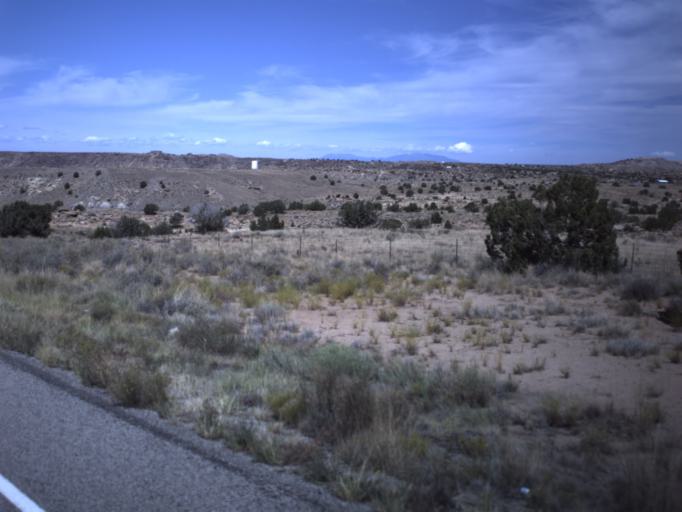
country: US
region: Colorado
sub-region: Montezuma County
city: Towaoc
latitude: 37.1916
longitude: -109.1370
